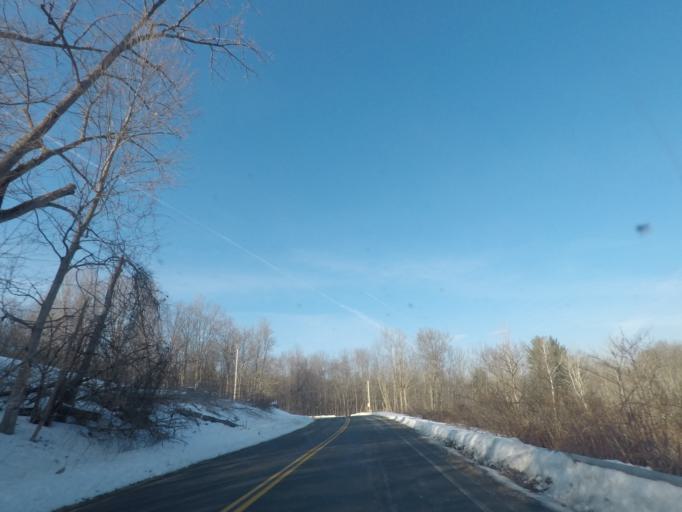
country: US
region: Massachusetts
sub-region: Berkshire County
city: Richmond
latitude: 42.5181
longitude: -73.3762
